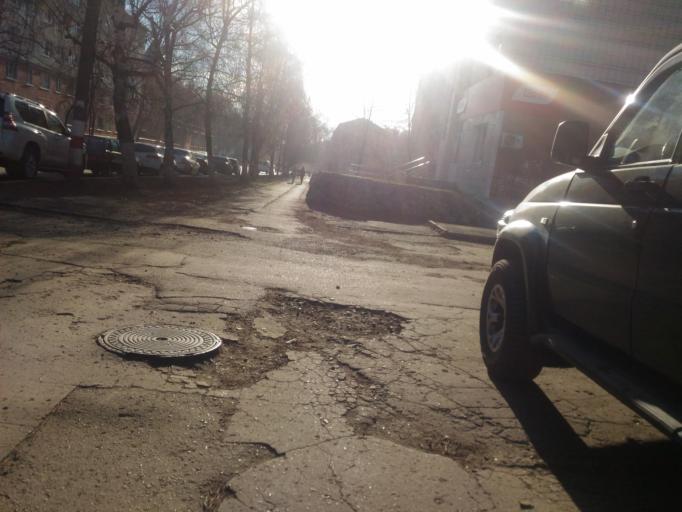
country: RU
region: Ulyanovsk
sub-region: Ulyanovskiy Rayon
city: Ulyanovsk
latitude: 54.3261
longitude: 48.3884
